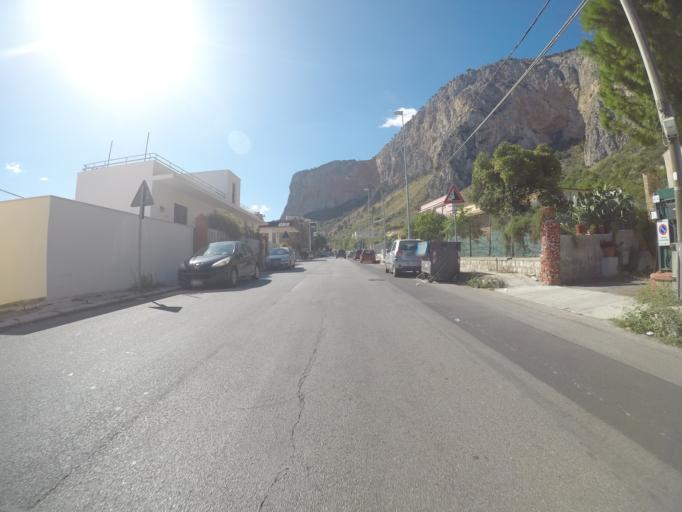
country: IT
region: Sicily
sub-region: Palermo
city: Palermo
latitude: 38.1682
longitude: 13.3664
